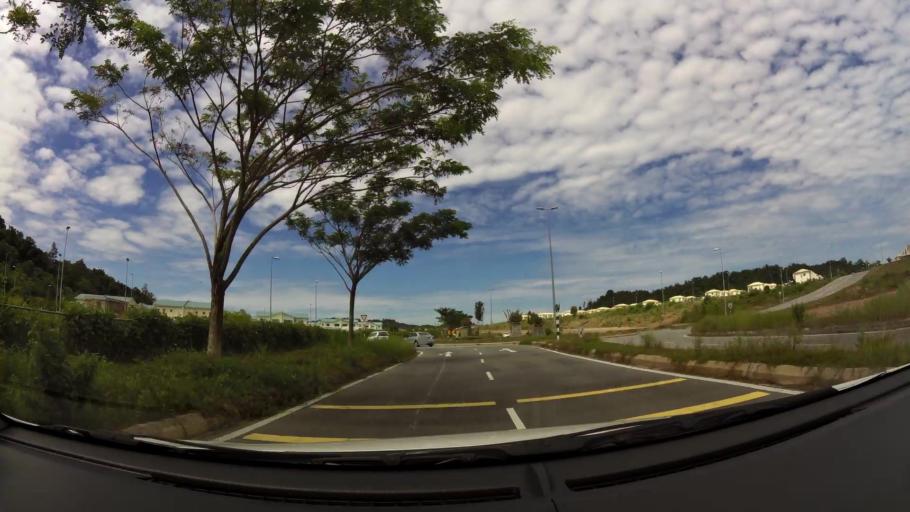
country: BN
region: Brunei and Muara
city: Bandar Seri Begawan
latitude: 4.9852
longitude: 115.0150
